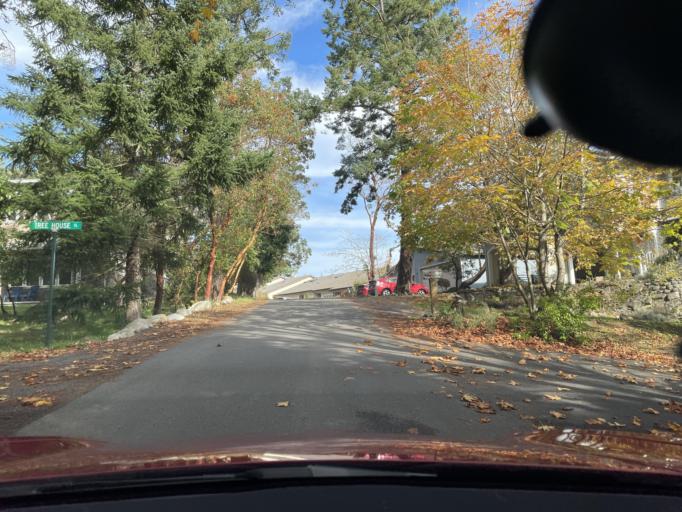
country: US
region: Washington
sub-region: San Juan County
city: Friday Harbor
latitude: 48.5310
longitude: -123.0284
